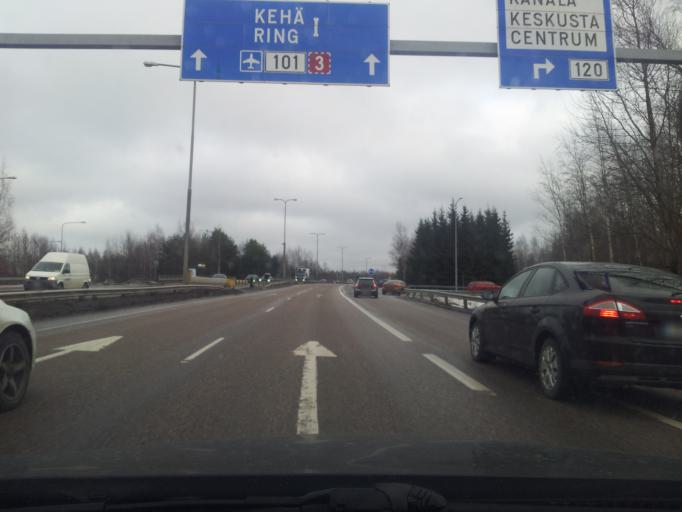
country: FI
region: Uusimaa
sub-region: Helsinki
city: Teekkarikylae
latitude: 60.2333
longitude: 24.8577
